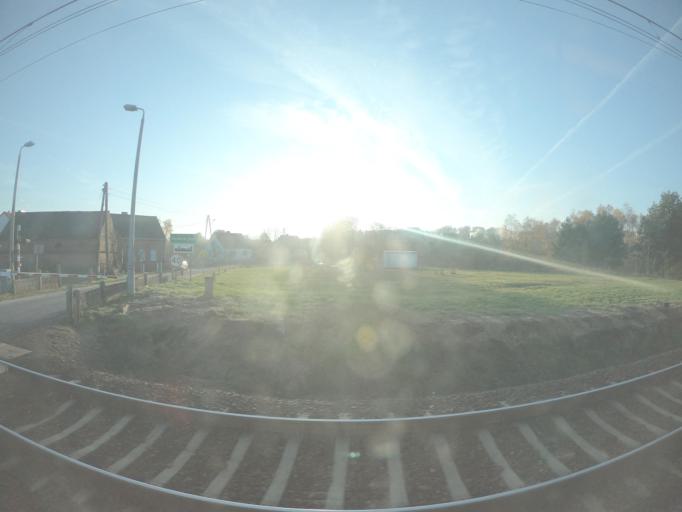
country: PL
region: Lubusz
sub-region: Powiat sulecinski
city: Torzym
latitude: 52.2555
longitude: 14.9511
